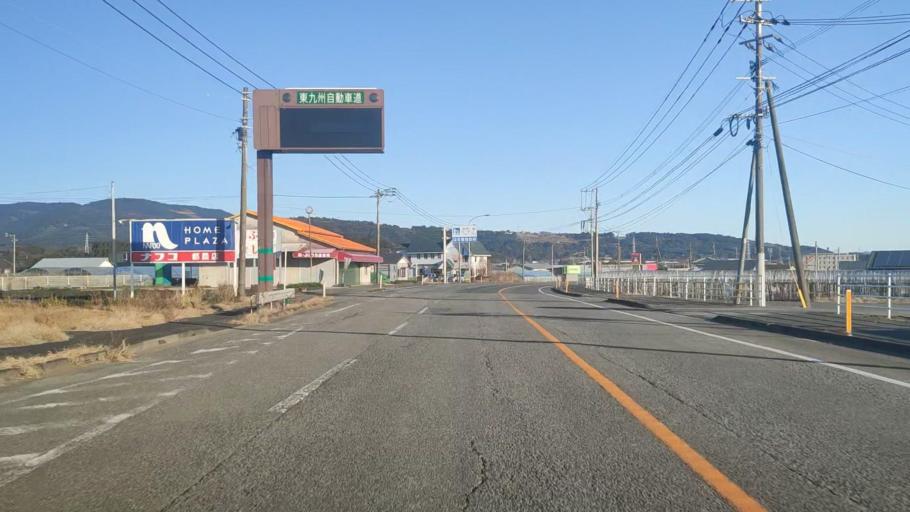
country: JP
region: Miyazaki
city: Takanabe
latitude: 32.2486
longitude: 131.5517
